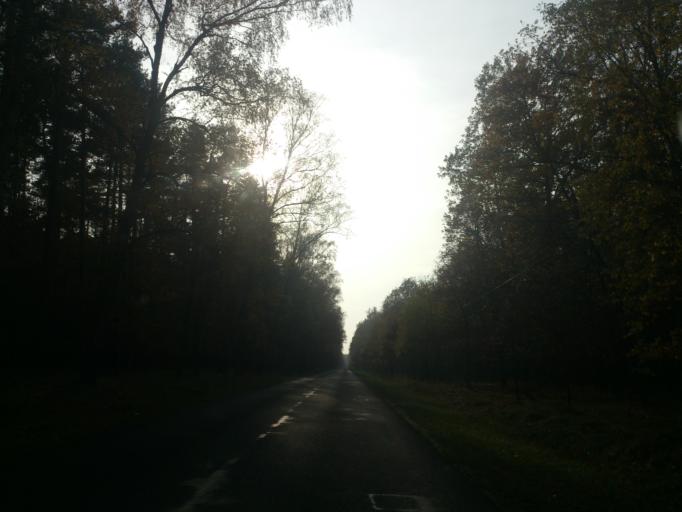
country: PL
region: Kujawsko-Pomorskie
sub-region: Powiat golubsko-dobrzynski
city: Ciechocin
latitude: 53.0872
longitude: 18.9856
